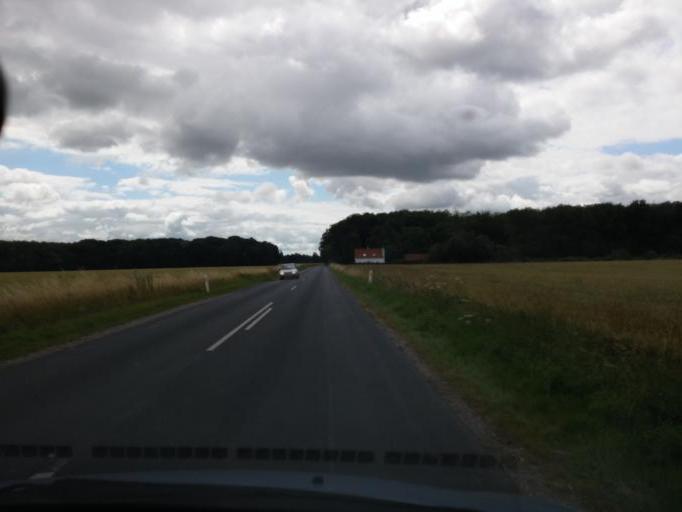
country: DK
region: South Denmark
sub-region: Kerteminde Kommune
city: Kerteminde
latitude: 55.4287
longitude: 10.6163
